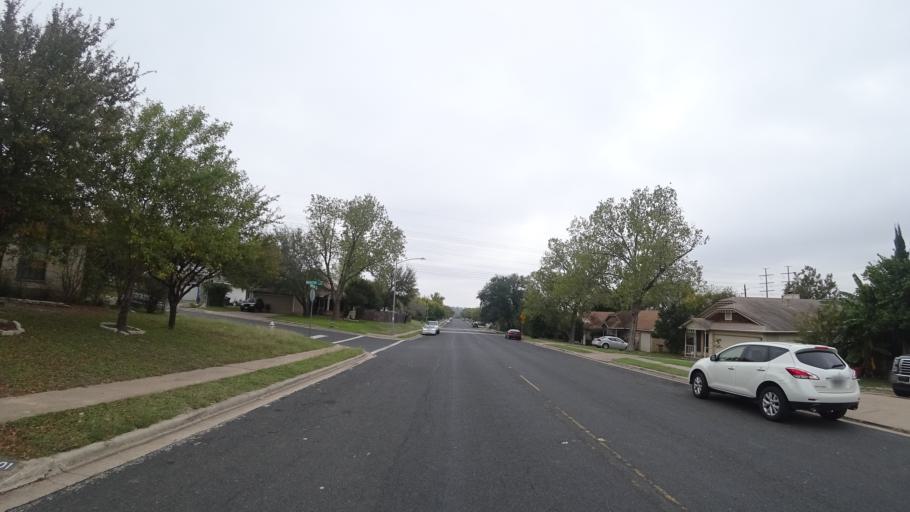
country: US
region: Texas
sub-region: Travis County
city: Wells Branch
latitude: 30.3877
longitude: -97.6575
